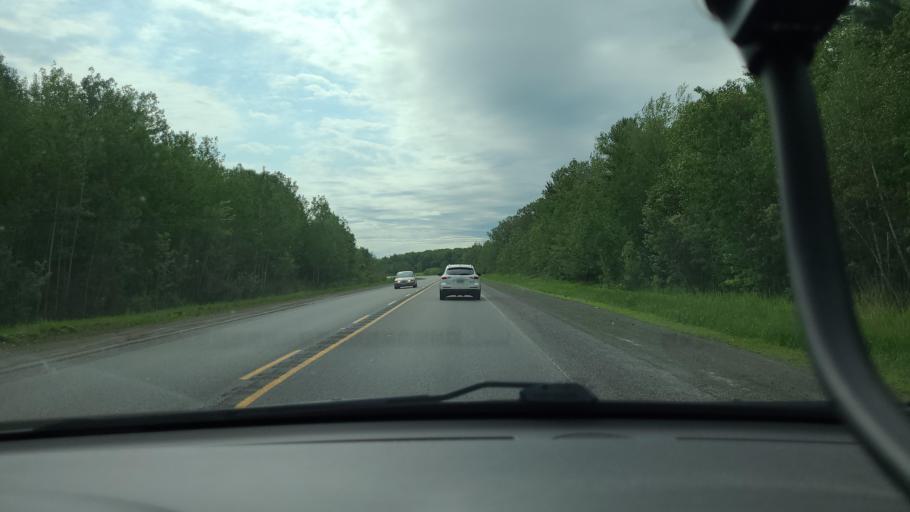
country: CA
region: Quebec
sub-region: Lanaudiere
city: Crabtree
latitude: 45.9625
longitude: -73.5134
